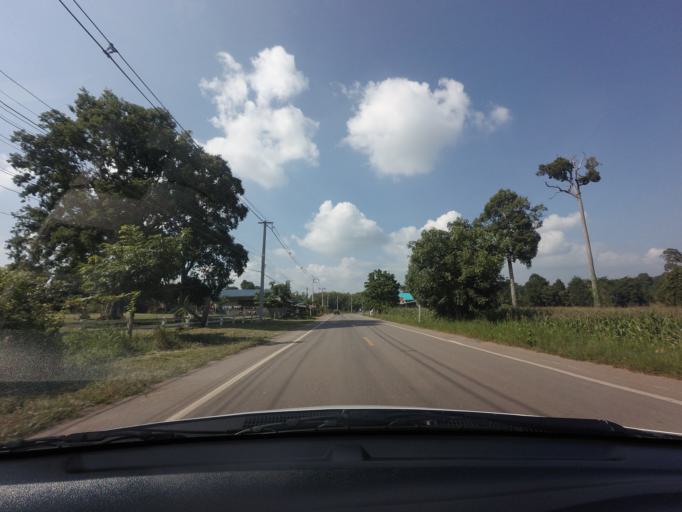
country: TH
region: Nakhon Ratchasima
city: Wang Nam Khiao
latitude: 14.4323
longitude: 101.6791
